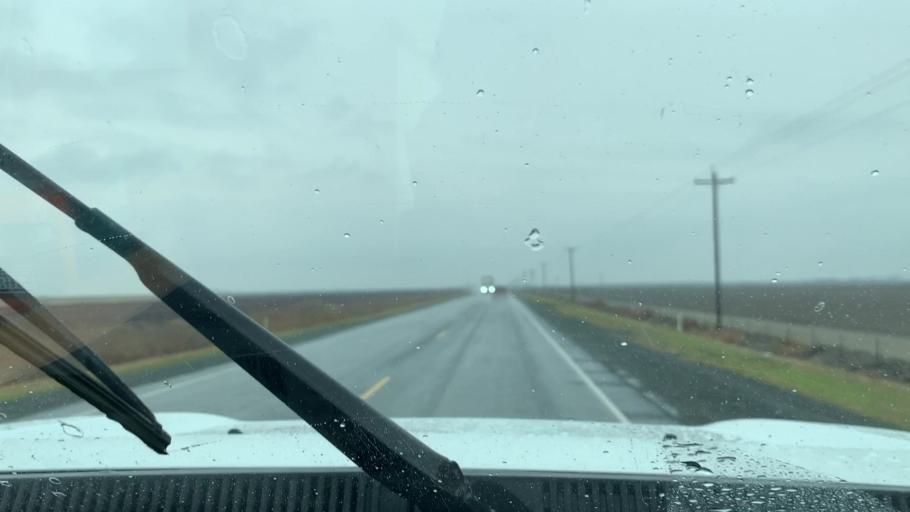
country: US
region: California
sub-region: Tulare County
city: Alpaugh
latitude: 35.9211
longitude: -119.4270
